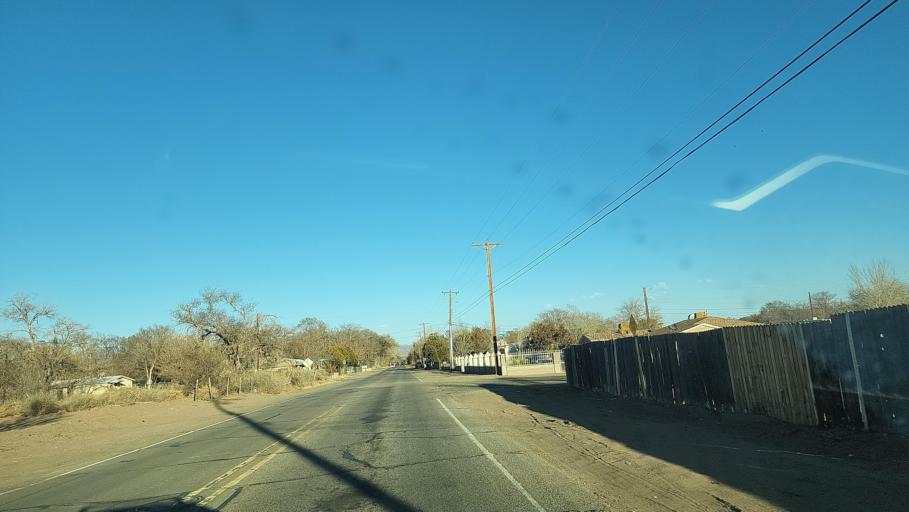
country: US
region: New Mexico
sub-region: Bernalillo County
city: South Valley
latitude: 35.0305
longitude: -106.7082
